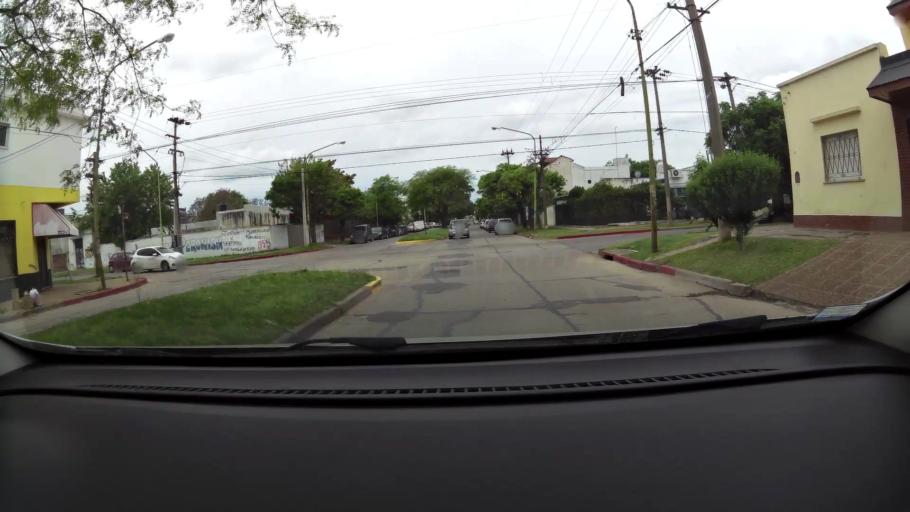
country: AR
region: Buenos Aires
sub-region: Partido de Campana
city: Campana
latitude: -34.1700
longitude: -58.9577
